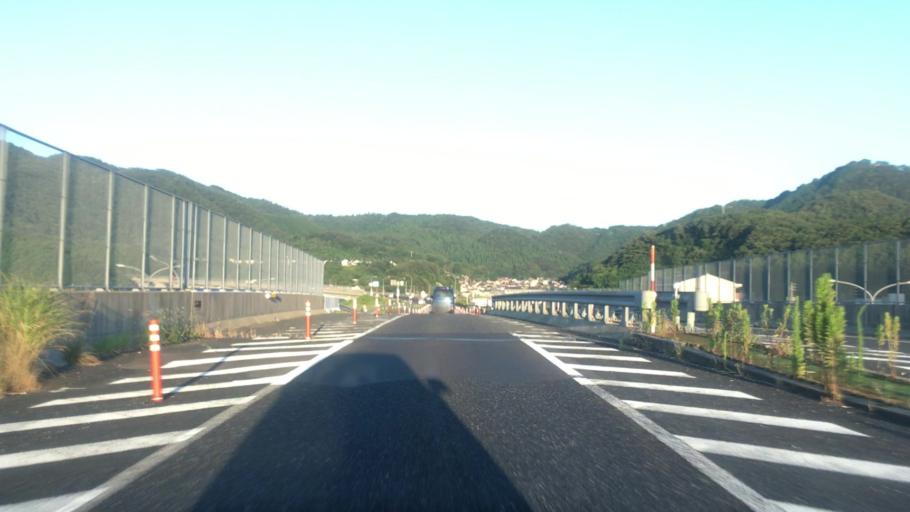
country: JP
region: Tottori
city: Tottori
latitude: 35.5229
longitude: 134.2286
